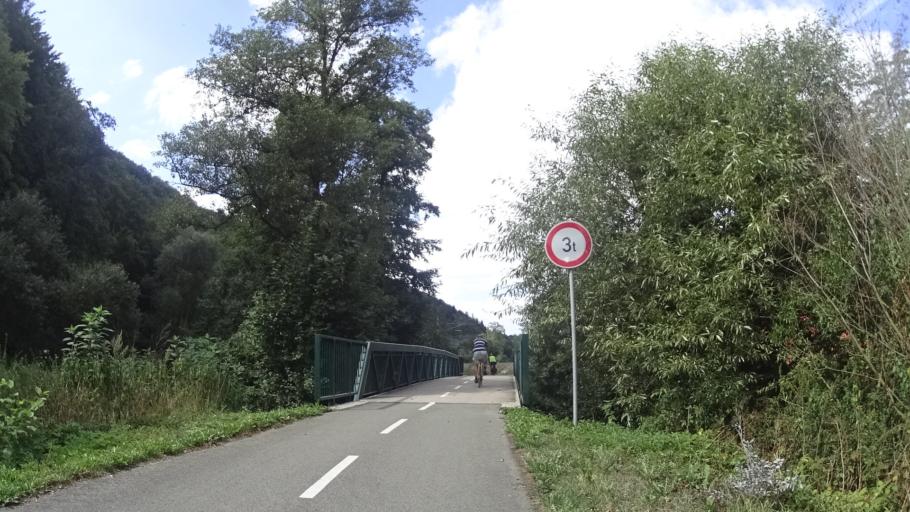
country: CZ
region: Pardubicky
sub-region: Okres Usti nad Orlici
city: Usti nad Orlici
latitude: 49.9878
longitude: 16.4408
